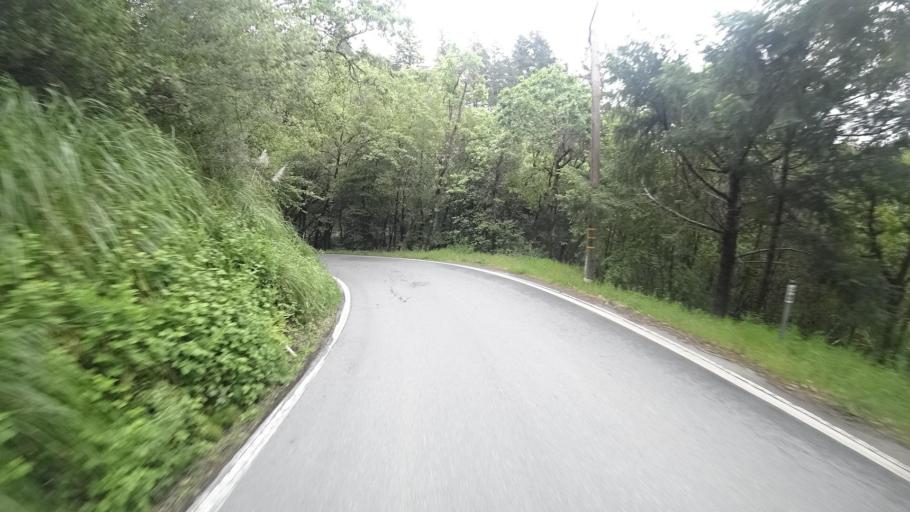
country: US
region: California
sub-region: Humboldt County
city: Willow Creek
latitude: 41.1948
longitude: -123.7191
